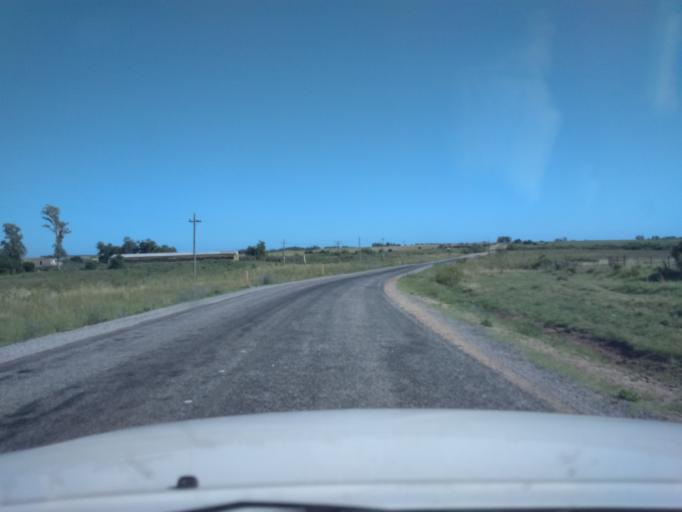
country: UY
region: Canelones
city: San Ramon
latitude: -34.2237
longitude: -55.9309
